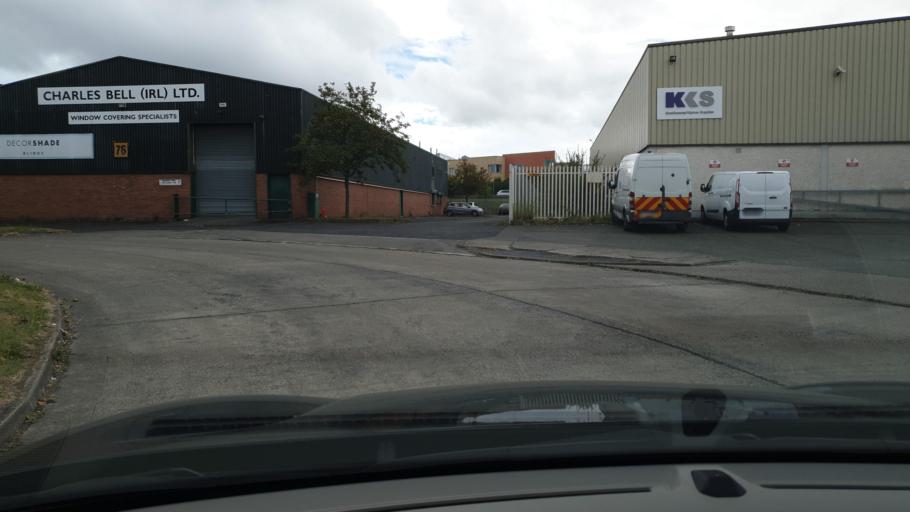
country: IE
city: Palmerstown
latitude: 53.3457
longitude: -6.3781
